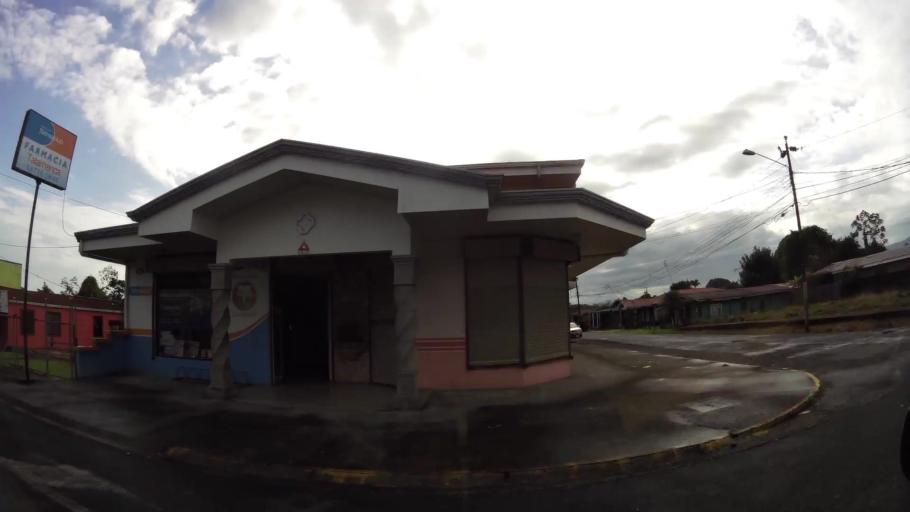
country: CR
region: Limon
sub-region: Canton de Guacimo
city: Guacimo
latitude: 10.2122
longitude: -83.6806
